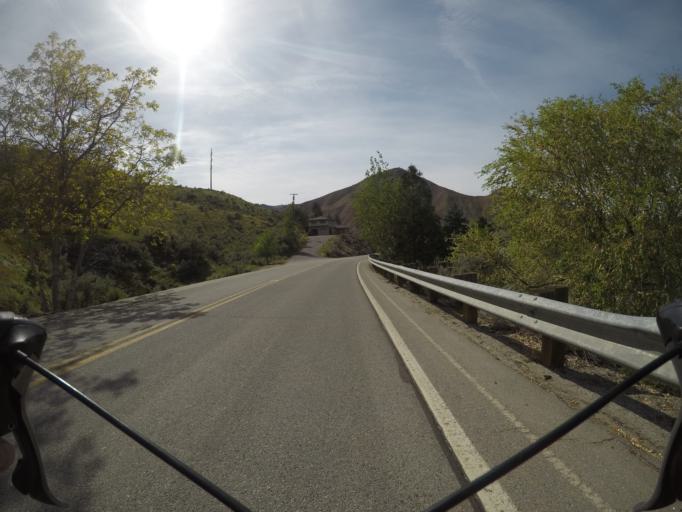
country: US
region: Washington
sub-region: Chelan County
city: West Wenatchee
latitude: 47.4120
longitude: -120.3439
